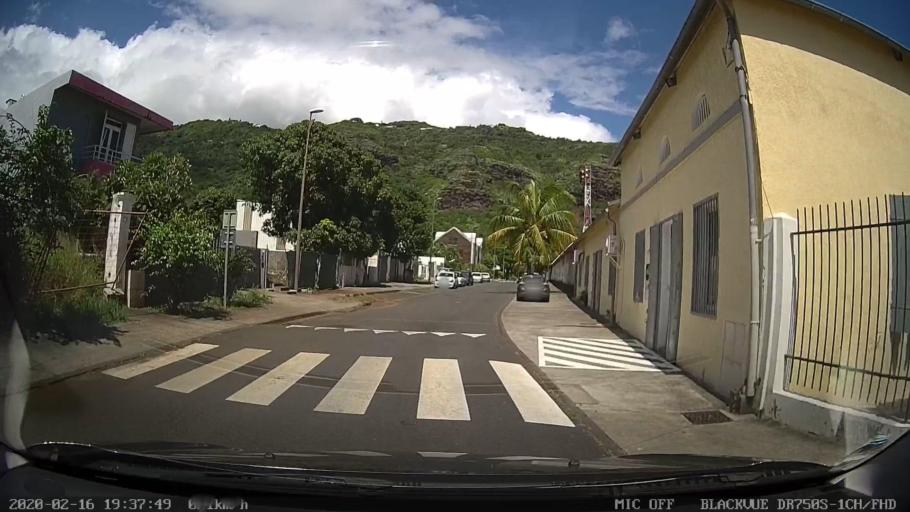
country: RE
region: Reunion
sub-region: Reunion
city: Saint-Denis
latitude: -20.8789
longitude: 55.4425
